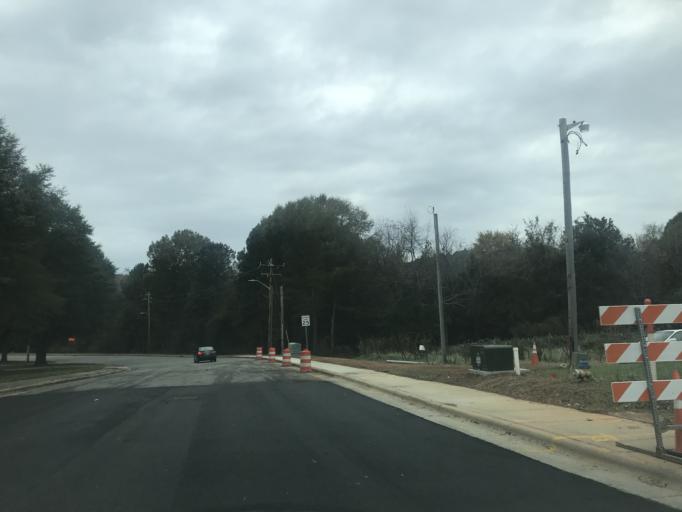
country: US
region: North Carolina
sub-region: Wake County
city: Wake Forest
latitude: 35.9717
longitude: -78.5131
